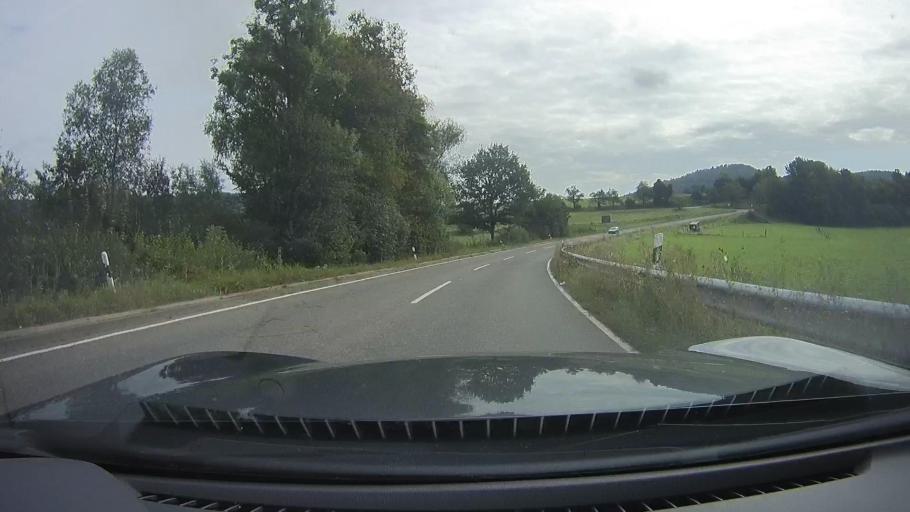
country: DE
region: Baden-Wuerttemberg
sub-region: Regierungsbezirk Stuttgart
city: Oberstenfeld
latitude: 49.0382
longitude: 9.3333
